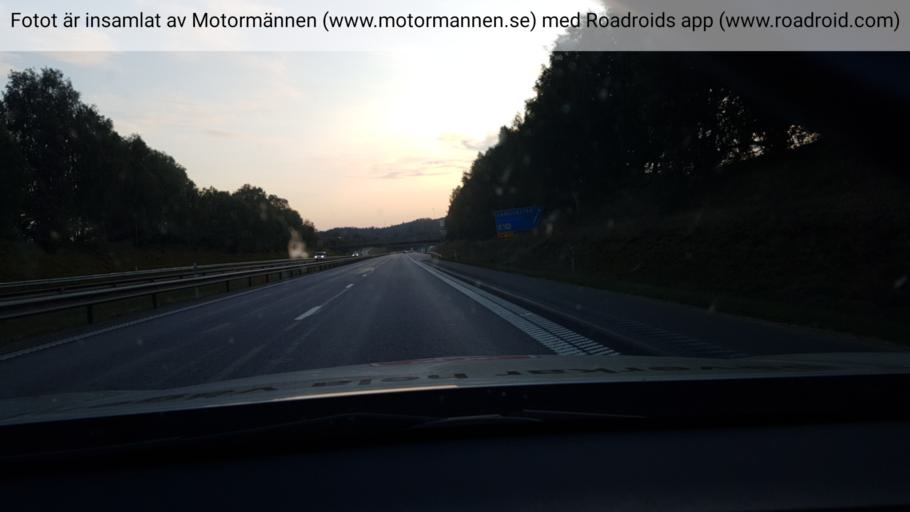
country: SE
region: Vaestra Goetaland
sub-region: Harryda Kommun
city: Landvetter
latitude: 57.6846
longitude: 12.2192
